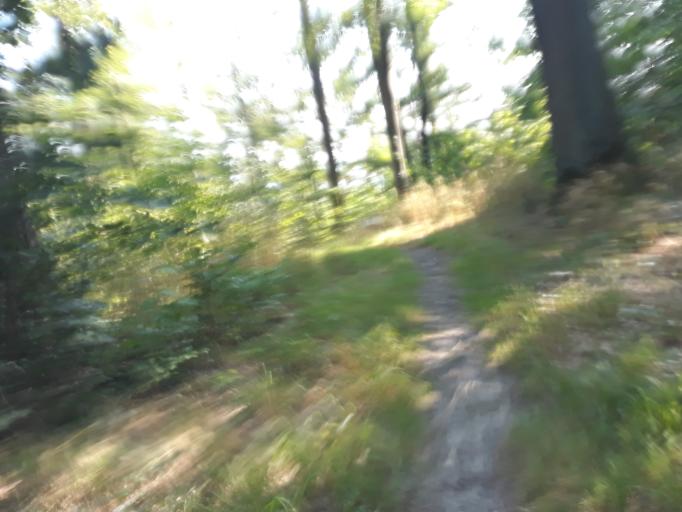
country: DE
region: Baden-Wuerttemberg
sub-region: Regierungsbezirk Stuttgart
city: Sindelfingen
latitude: 48.6880
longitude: 9.0360
